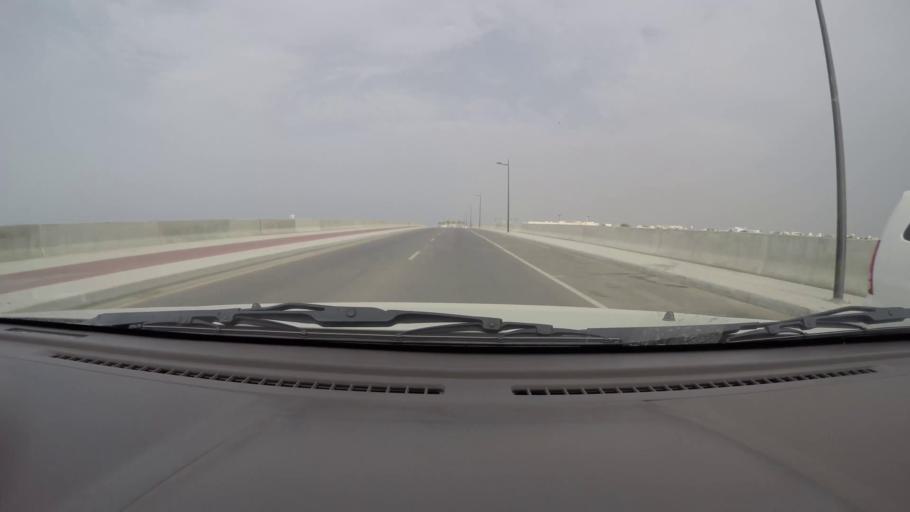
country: OM
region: Muhafazat Masqat
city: As Sib al Jadidah
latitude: 23.6907
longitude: 58.1711
